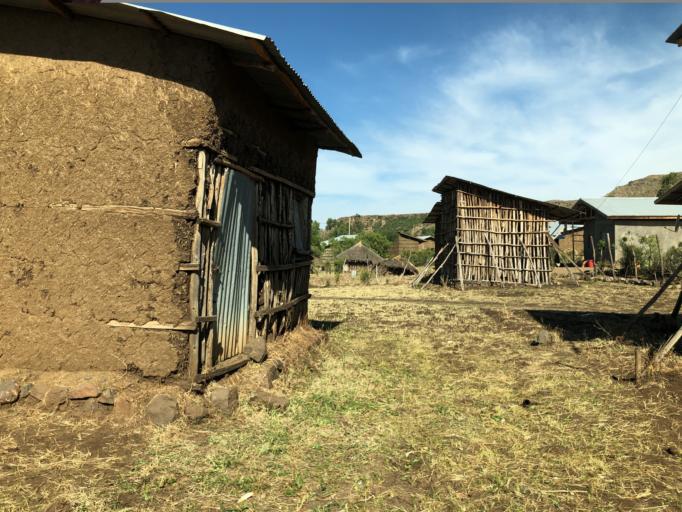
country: ET
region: Amhara
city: Lalibela
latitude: 11.9979
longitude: 39.0609
